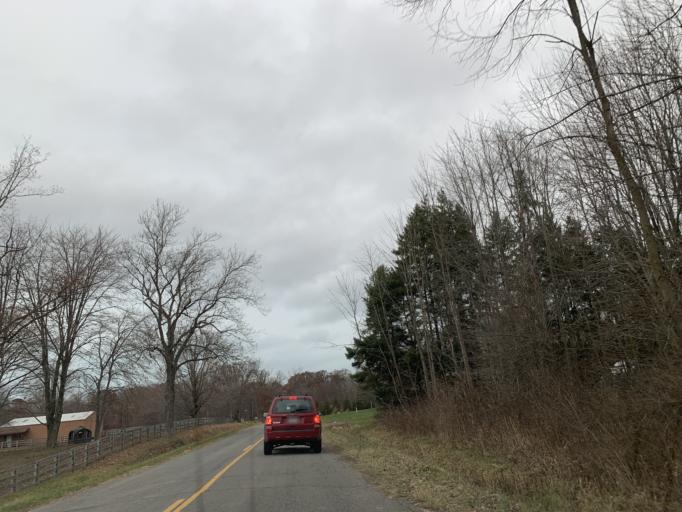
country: US
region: Michigan
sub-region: Berrien County
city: Three Oaks
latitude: 41.8122
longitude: -86.6683
